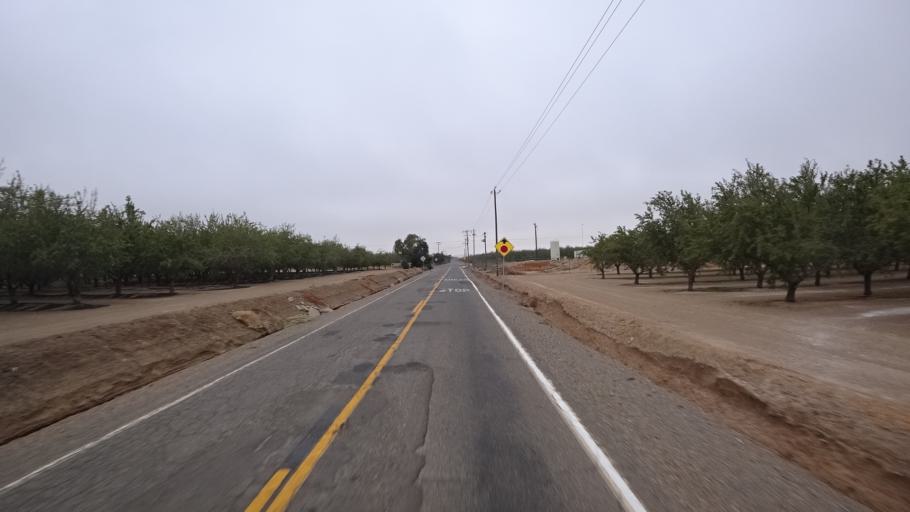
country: US
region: California
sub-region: Colusa County
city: Arbuckle
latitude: 38.9259
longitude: -122.0595
